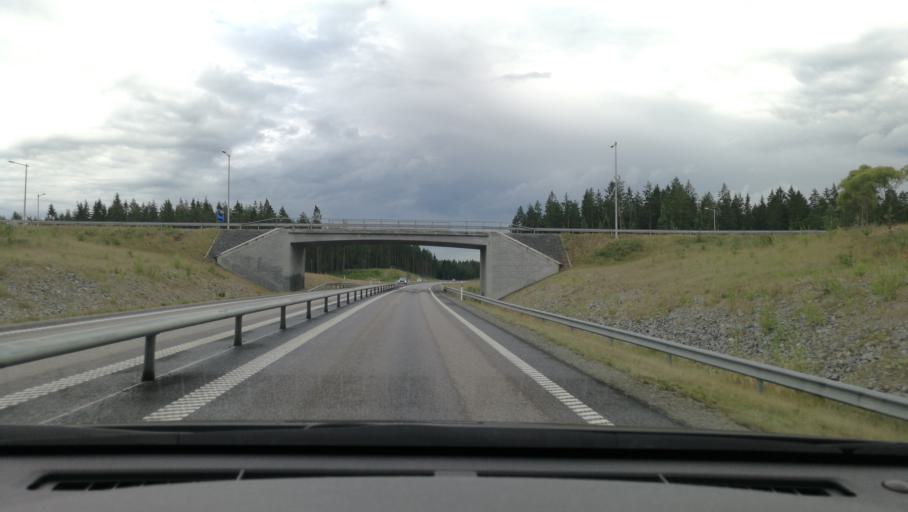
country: SE
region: Soedermanland
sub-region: Katrineholms Kommun
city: Katrineholm
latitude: 58.9944
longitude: 16.2592
